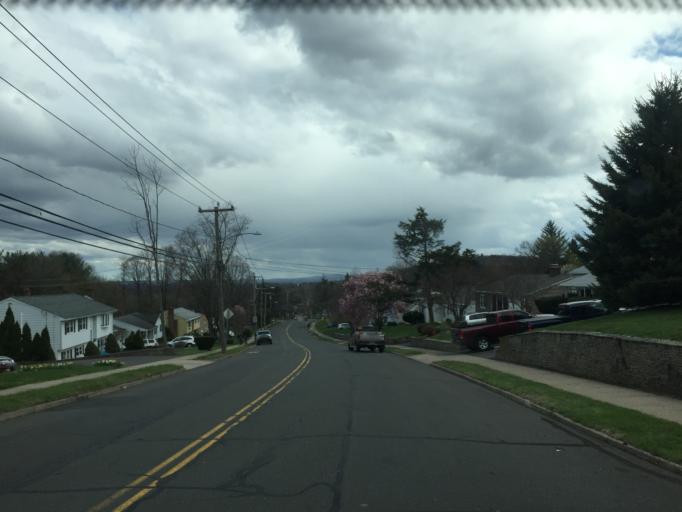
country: US
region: Connecticut
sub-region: Hartford County
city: New Britain
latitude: 41.7105
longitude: -72.7766
